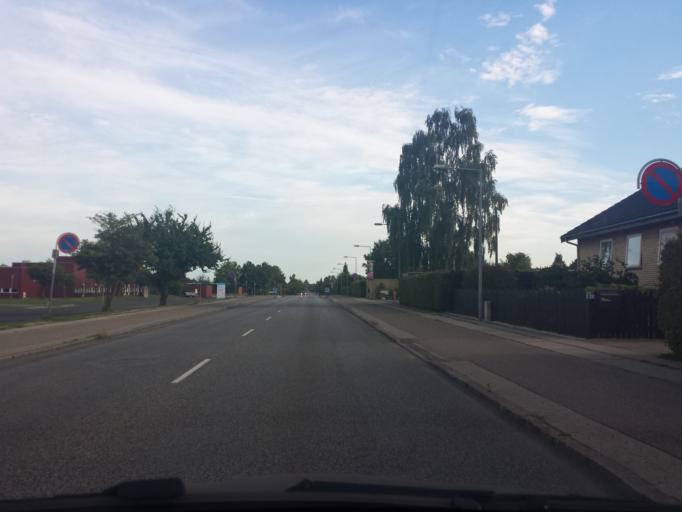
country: DK
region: Capital Region
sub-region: Ballerup Kommune
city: Ballerup
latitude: 55.7169
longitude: 12.3990
